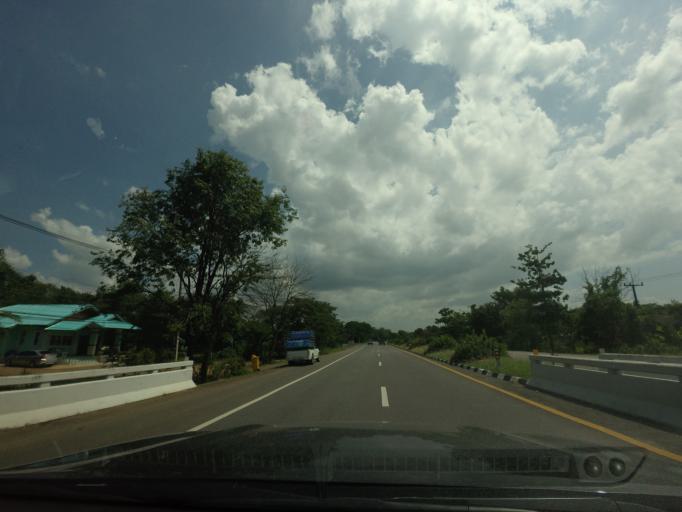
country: TH
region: Phetchabun
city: Phetchabun
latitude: 16.2274
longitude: 101.0875
